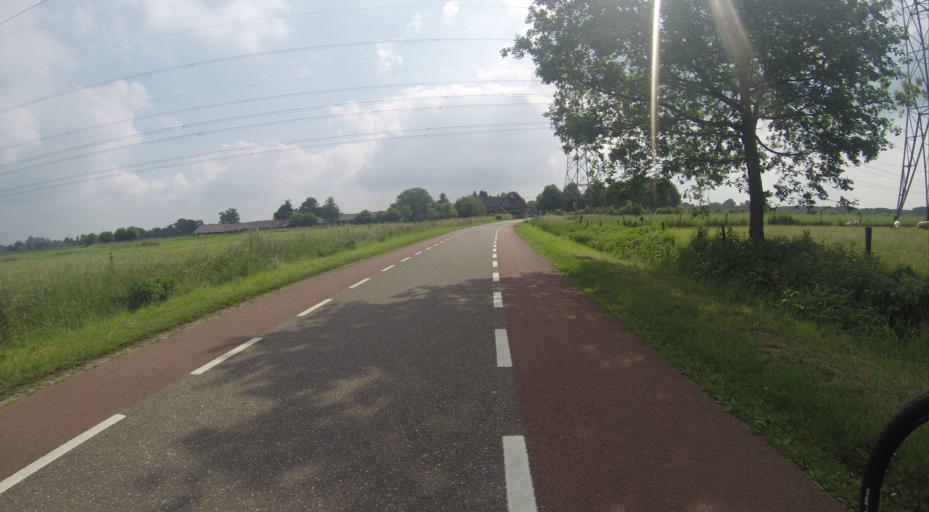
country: NL
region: Gelderland
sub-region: Gemeente Zutphen
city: Leesten
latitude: 52.1068
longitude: 6.2295
